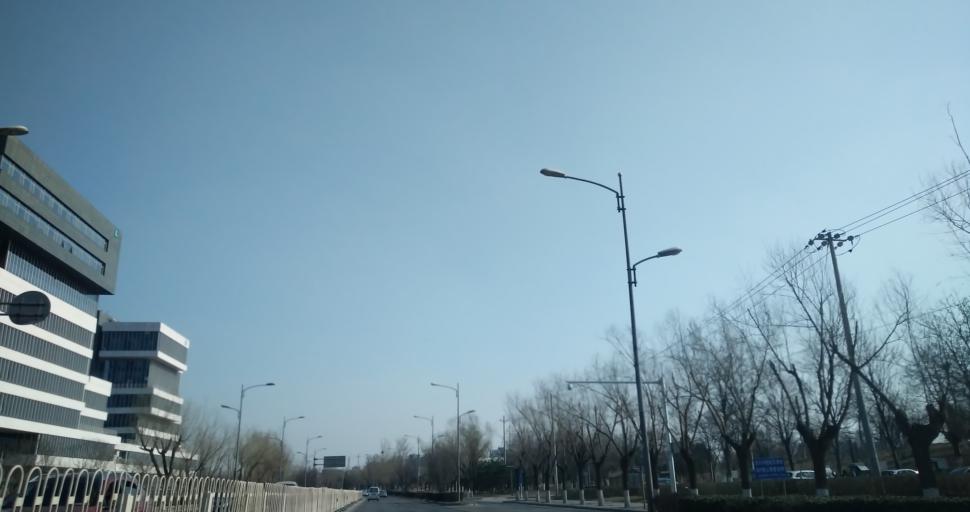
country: CN
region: Beijing
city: Jiugong
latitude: 39.7807
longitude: 116.4890
